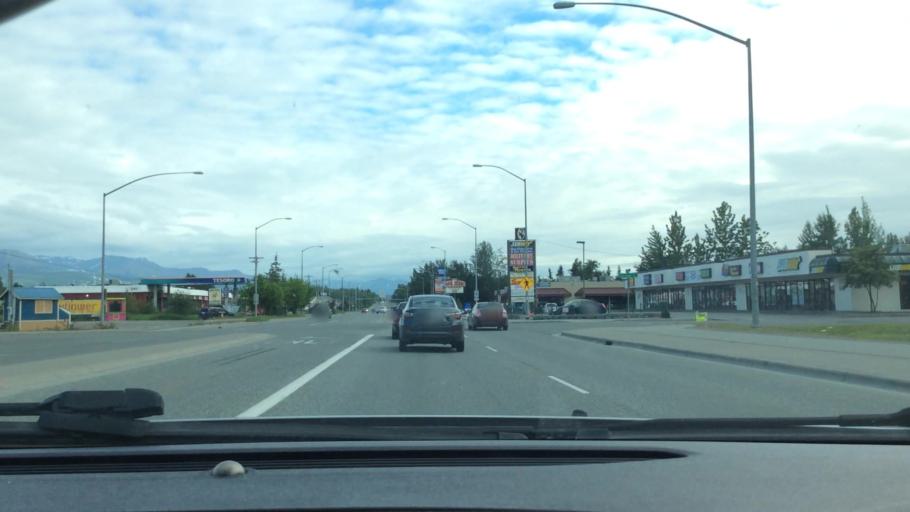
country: US
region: Alaska
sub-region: Anchorage Municipality
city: Anchorage
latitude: 61.2229
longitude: -149.7786
